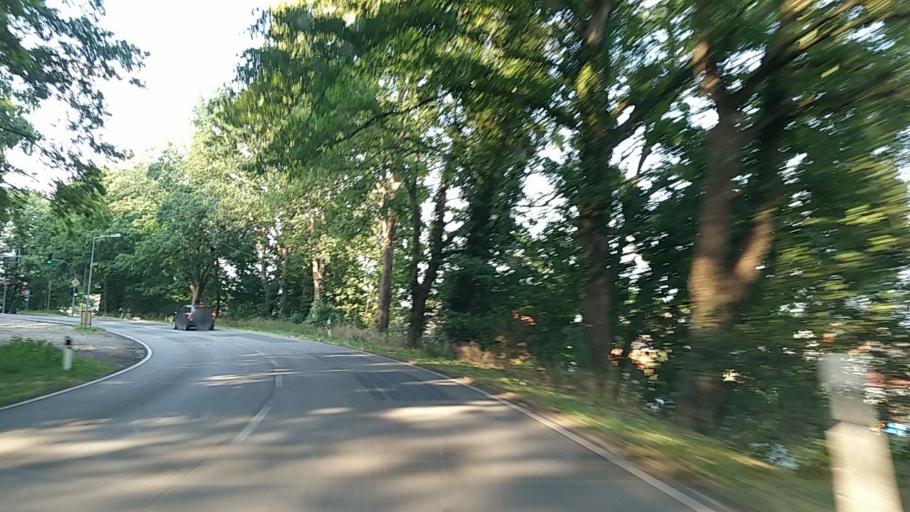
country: DE
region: Lower Saxony
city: Neu Wulmstorf
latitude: 53.4573
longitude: 9.8008
